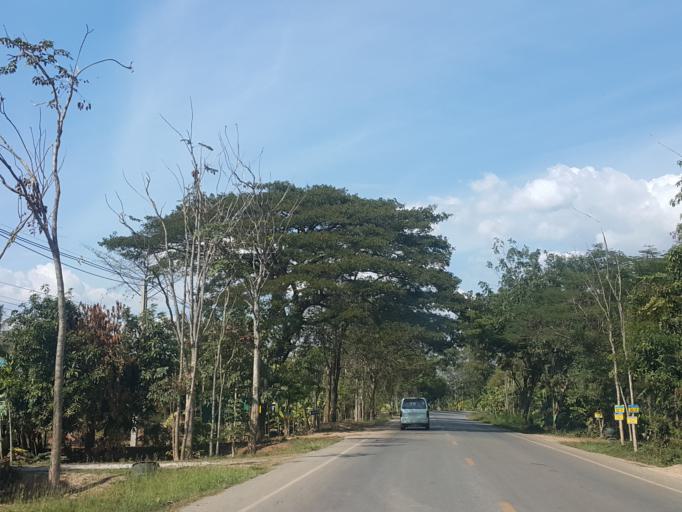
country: TH
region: Sukhothai
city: Sawankhalok
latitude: 17.2740
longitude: 99.8301
